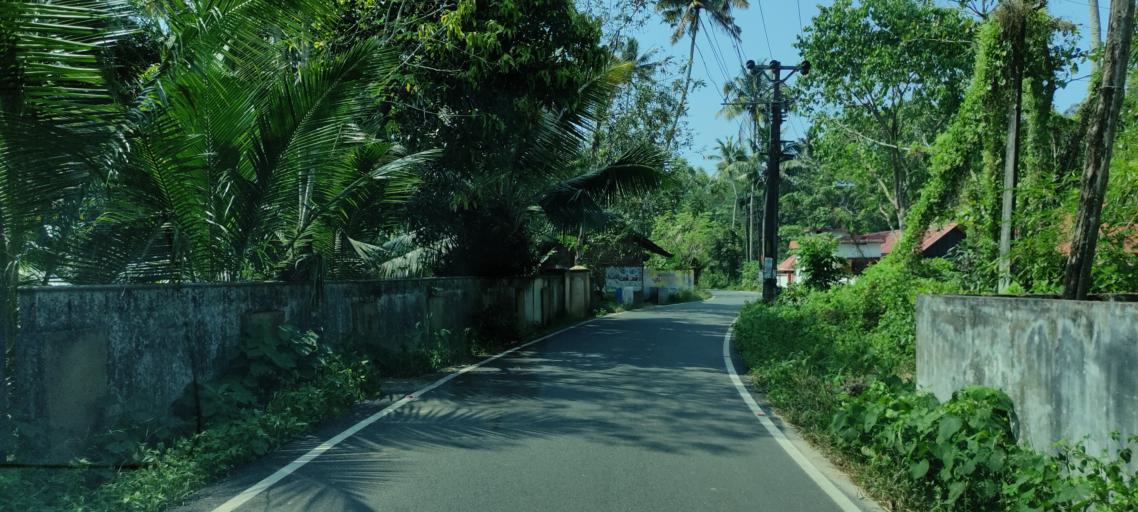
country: IN
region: Kerala
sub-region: Alappuzha
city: Alleppey
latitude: 9.5550
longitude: 76.3136
